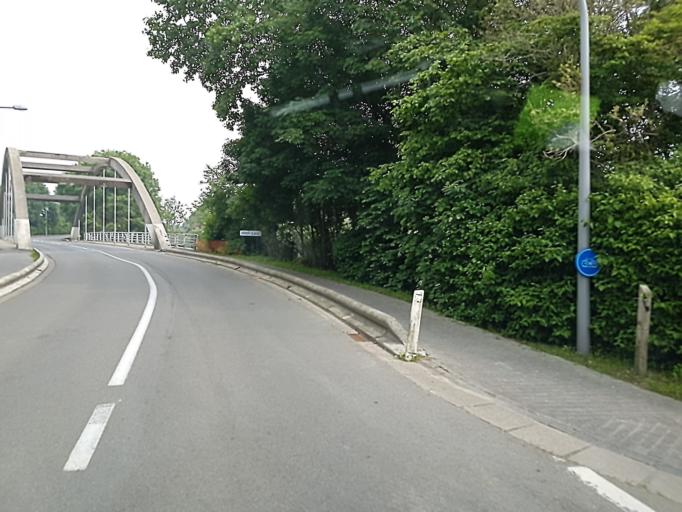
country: BE
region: Flanders
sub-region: Provincie West-Vlaanderen
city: Kortrijk
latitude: 50.8176
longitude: 3.2321
